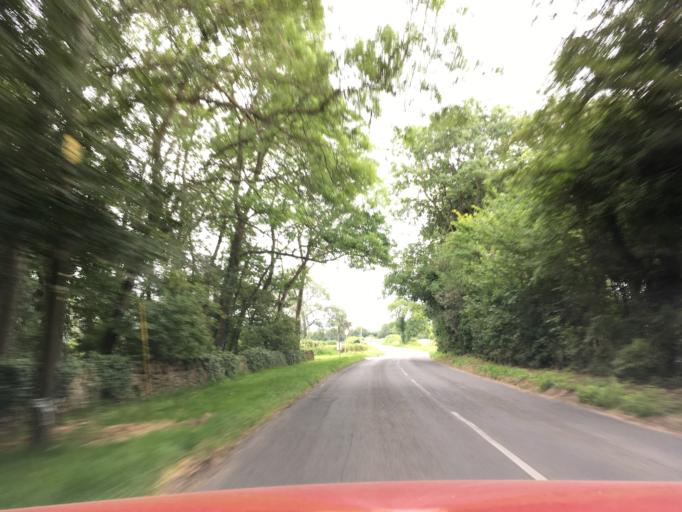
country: GB
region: England
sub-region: Oxfordshire
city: Chipping Norton
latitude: 51.9279
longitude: -1.5765
